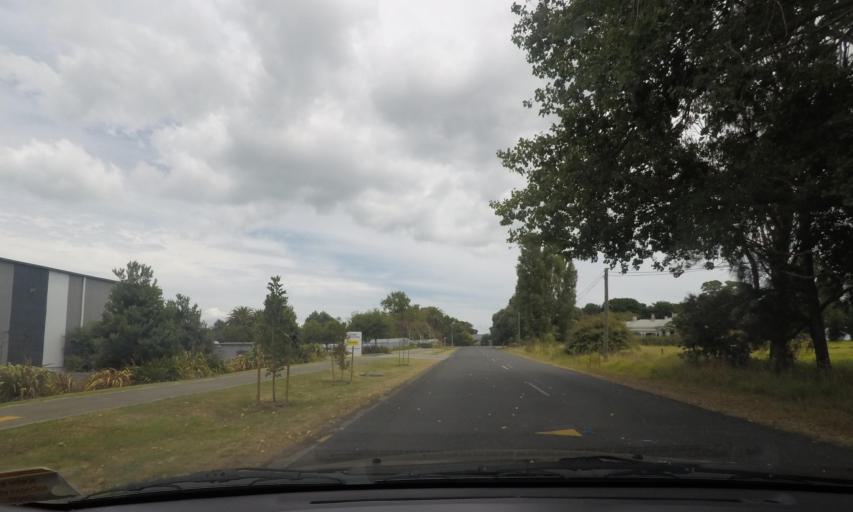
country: NZ
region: Auckland
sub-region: Auckland
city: Mangere
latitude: -36.9908
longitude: 174.7588
